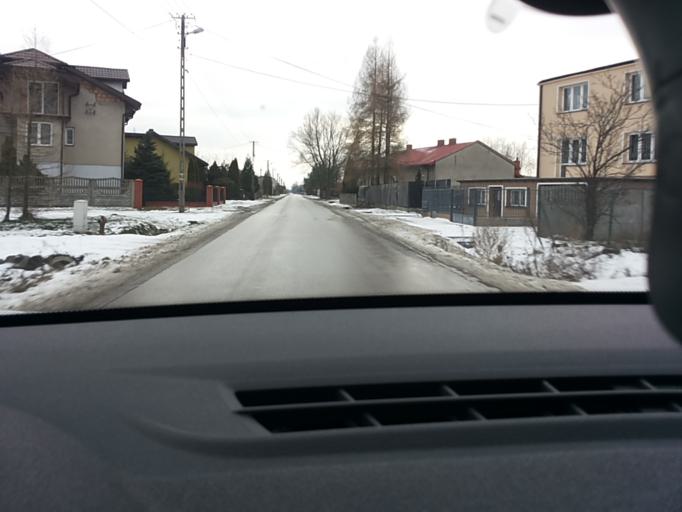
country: PL
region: Lodz Voivodeship
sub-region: Powiat skierniewicki
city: Makow
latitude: 52.0059
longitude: 20.0708
